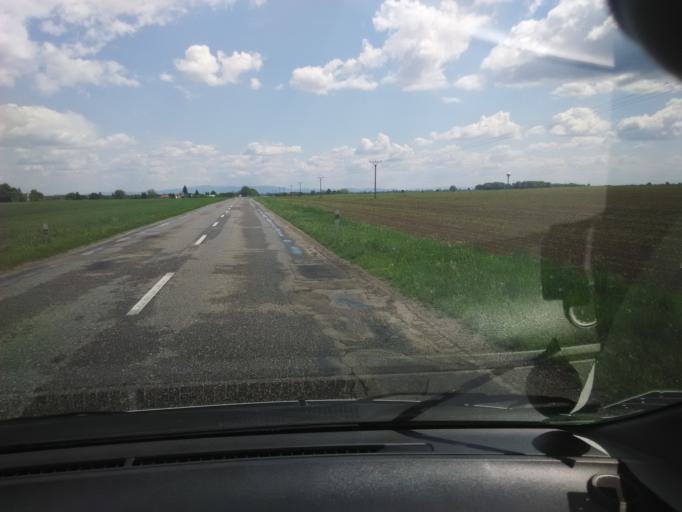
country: SK
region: Nitriansky
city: Levice
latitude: 48.1707
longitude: 18.5400
